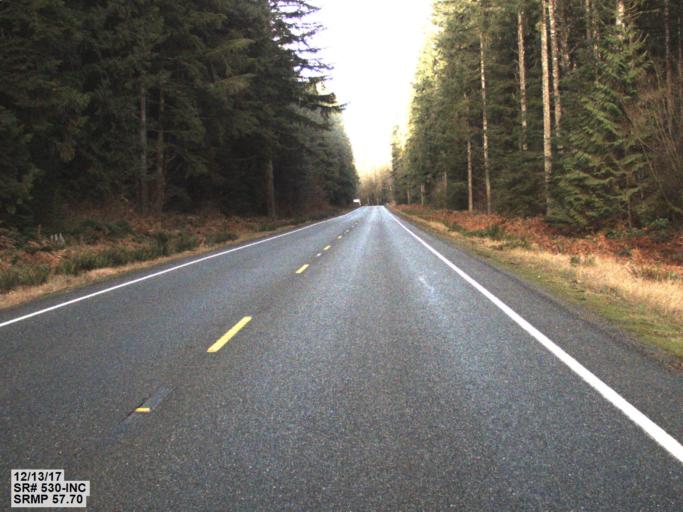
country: US
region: Washington
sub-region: Snohomish County
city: Darrington
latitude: 48.3607
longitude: -121.5398
